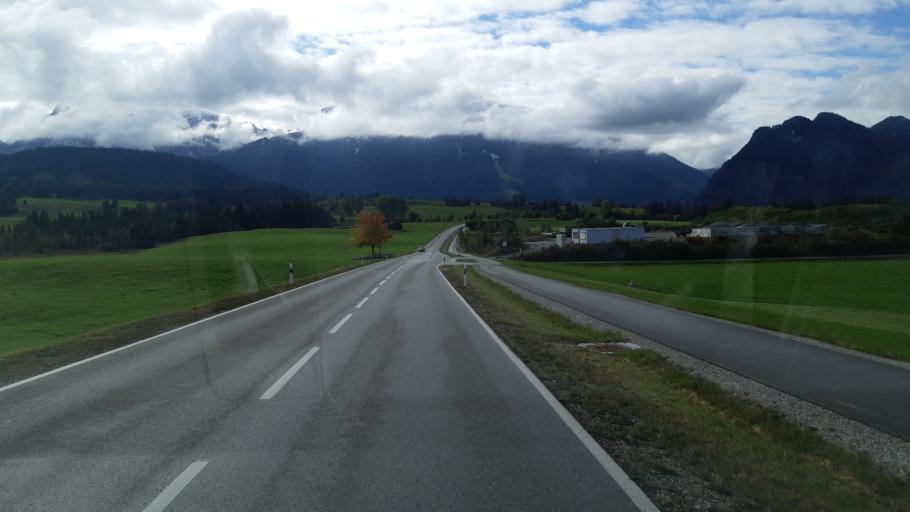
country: DE
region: Bavaria
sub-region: Swabia
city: Pfronten
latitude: 47.5955
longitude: 10.5794
